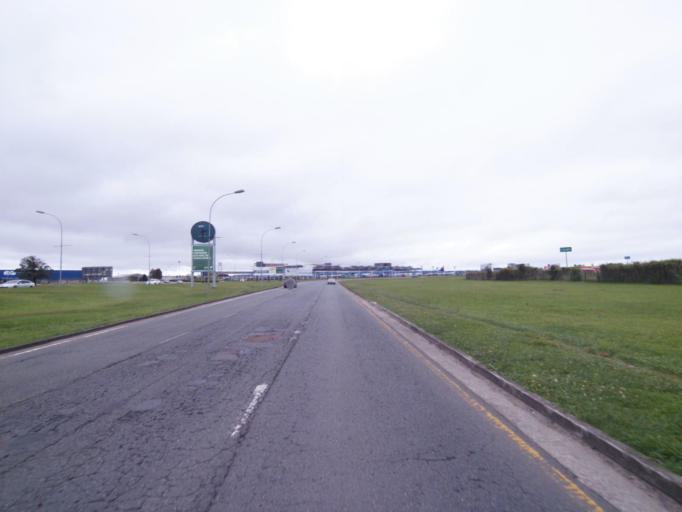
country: BR
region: Parana
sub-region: Sao Jose Dos Pinhais
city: Sao Jose dos Pinhais
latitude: -25.5365
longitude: -49.1790
